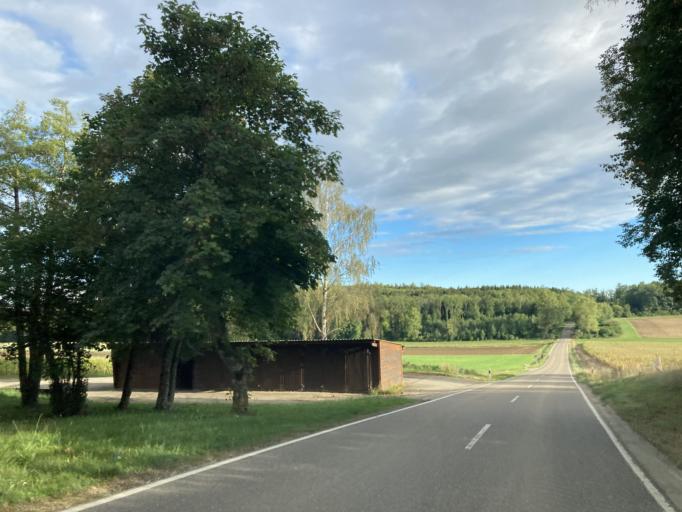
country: DE
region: Bavaria
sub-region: Swabia
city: Modingen
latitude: 48.7031
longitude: 10.4362
